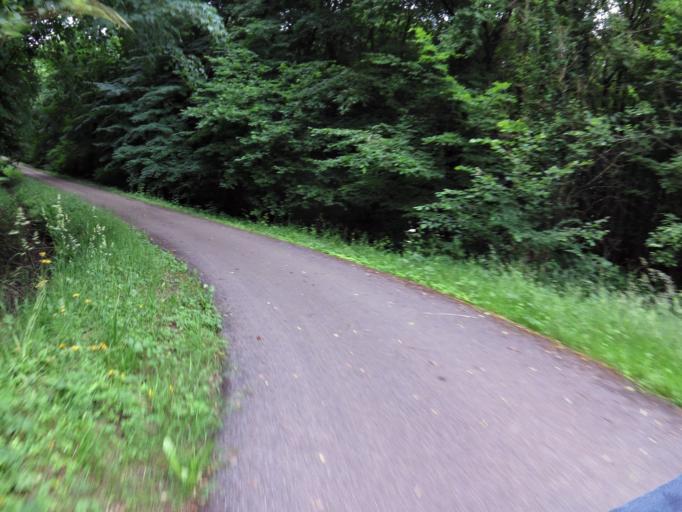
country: FR
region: Champagne-Ardenne
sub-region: Departement de la Haute-Marne
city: Montier-en-Der
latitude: 48.5432
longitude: 4.8153
